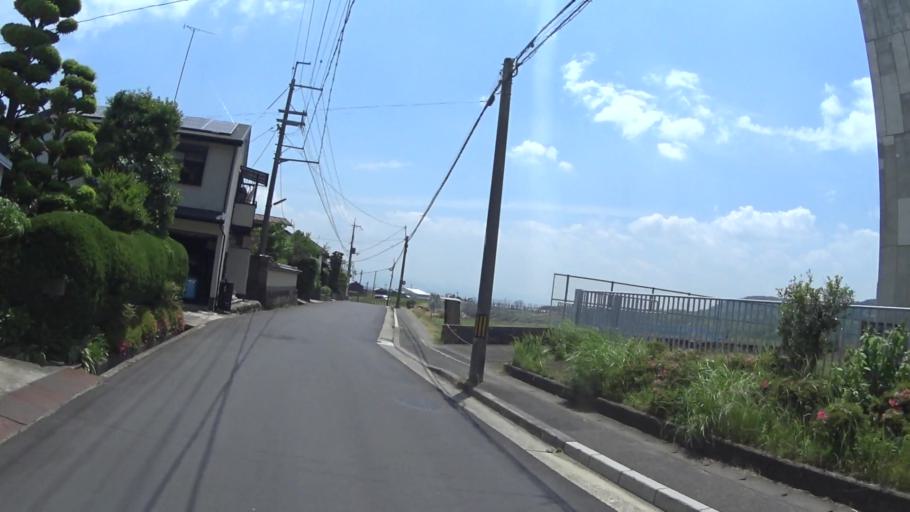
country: JP
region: Kyoto
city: Muko
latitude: 34.9573
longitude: 135.6611
